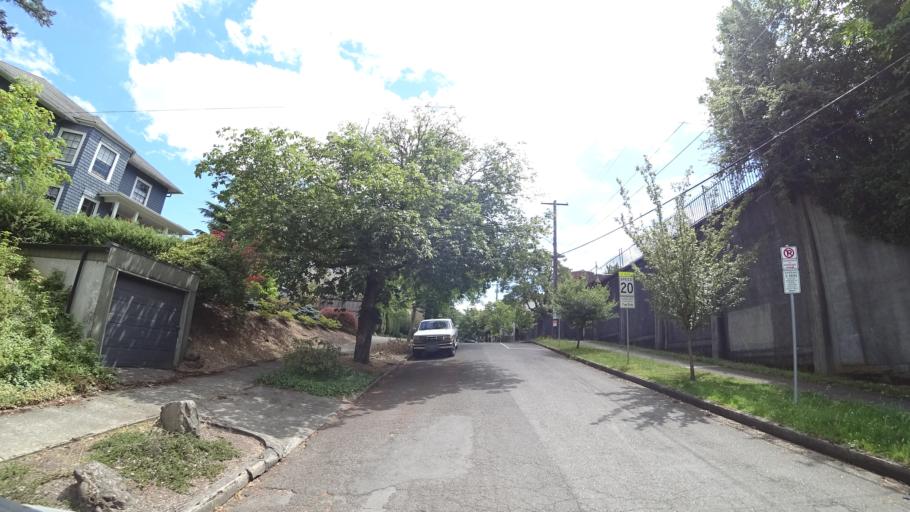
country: US
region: Oregon
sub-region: Multnomah County
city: Portland
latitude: 45.5105
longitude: -122.7006
